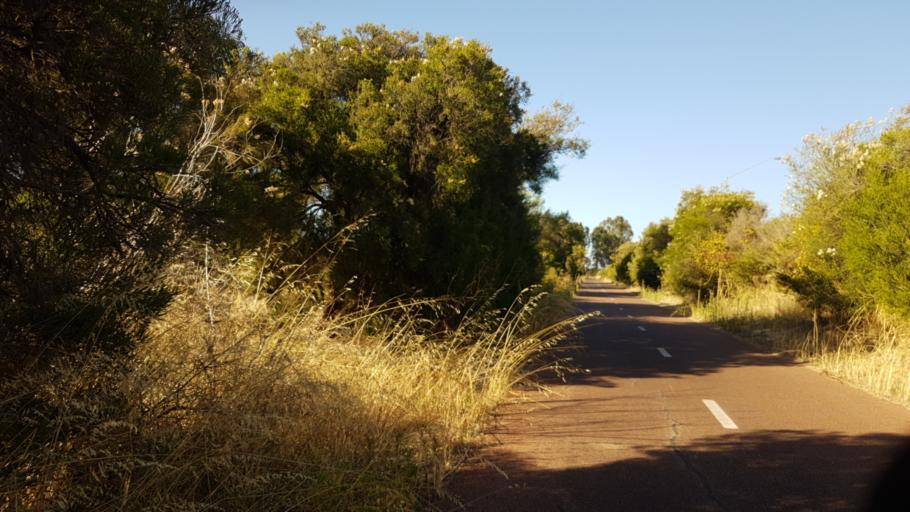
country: AU
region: Western Australia
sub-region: Kwinana
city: Wellard
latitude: -32.2903
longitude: 115.8361
